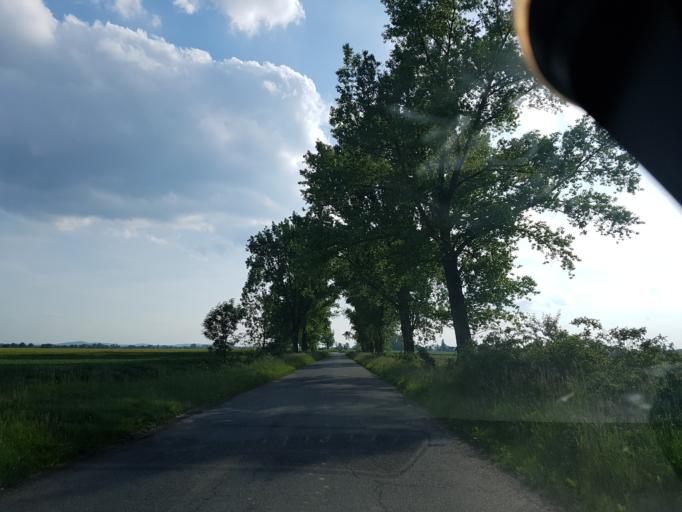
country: PL
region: Lower Silesian Voivodeship
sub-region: Powiat strzelinski
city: Wiazow
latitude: 50.8444
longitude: 17.2329
